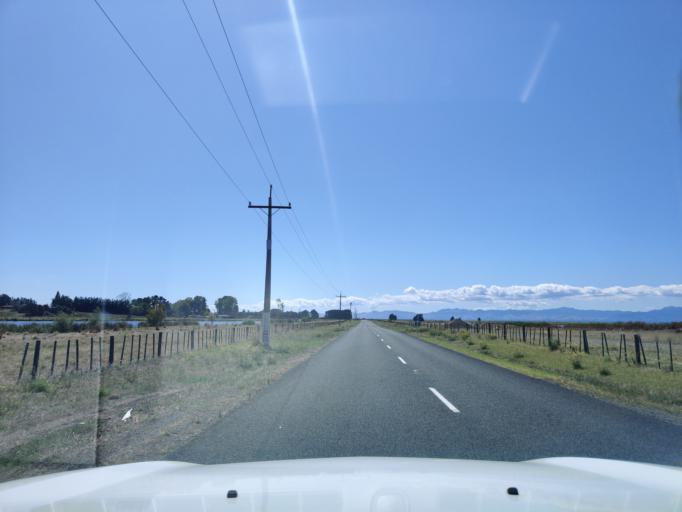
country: NZ
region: Waikato
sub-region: Thames-Coromandel District
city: Thames
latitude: -37.0597
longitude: 175.2984
